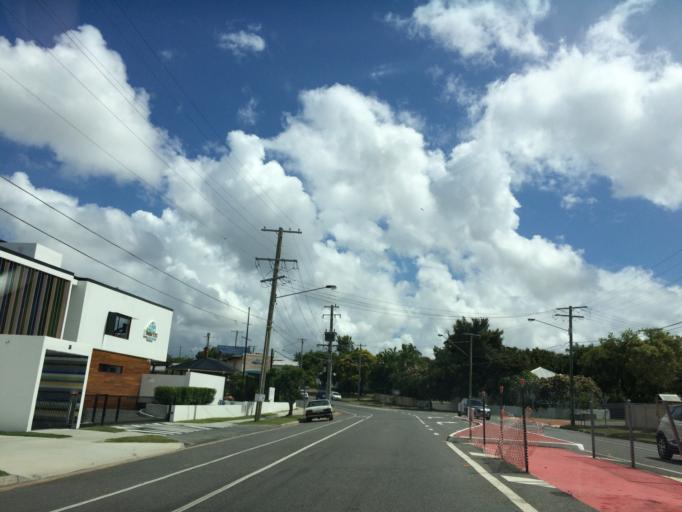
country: AU
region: Queensland
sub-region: Brisbane
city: Camp Hill
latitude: -27.4907
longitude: 153.0645
